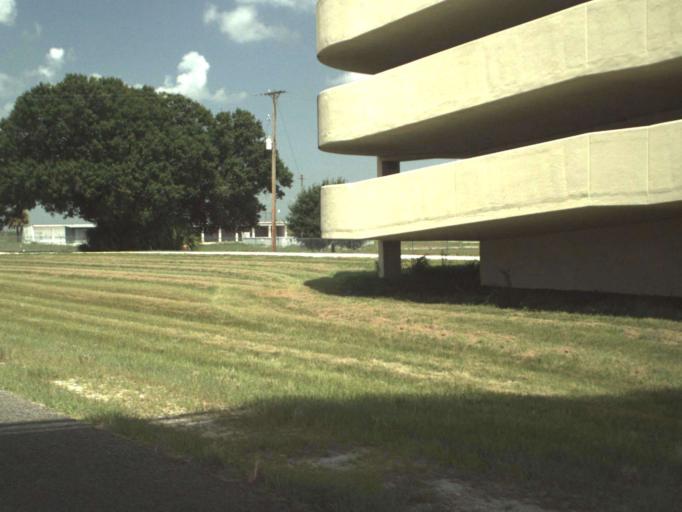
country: US
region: Florida
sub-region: Saint Lucie County
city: Fort Pierce South
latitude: 27.3761
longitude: -80.4871
